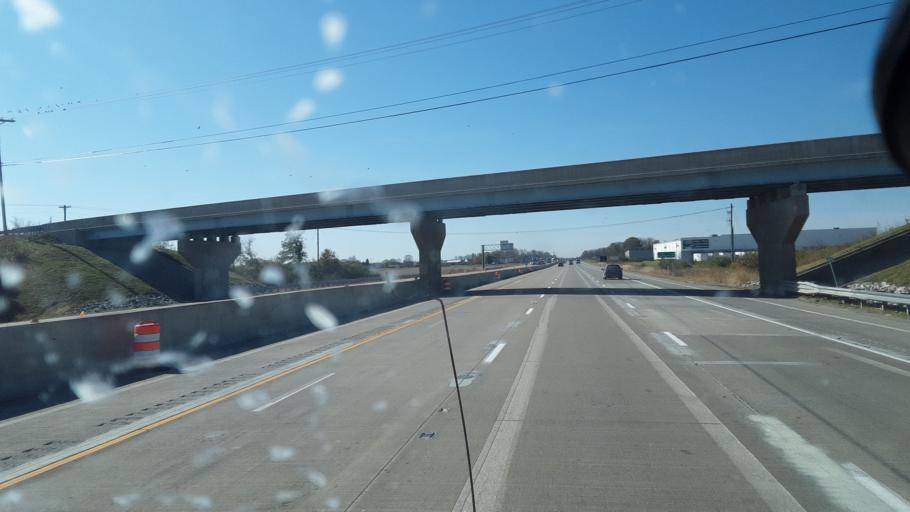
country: US
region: Indiana
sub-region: Marion County
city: Cumberland
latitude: 39.8136
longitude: -85.9337
